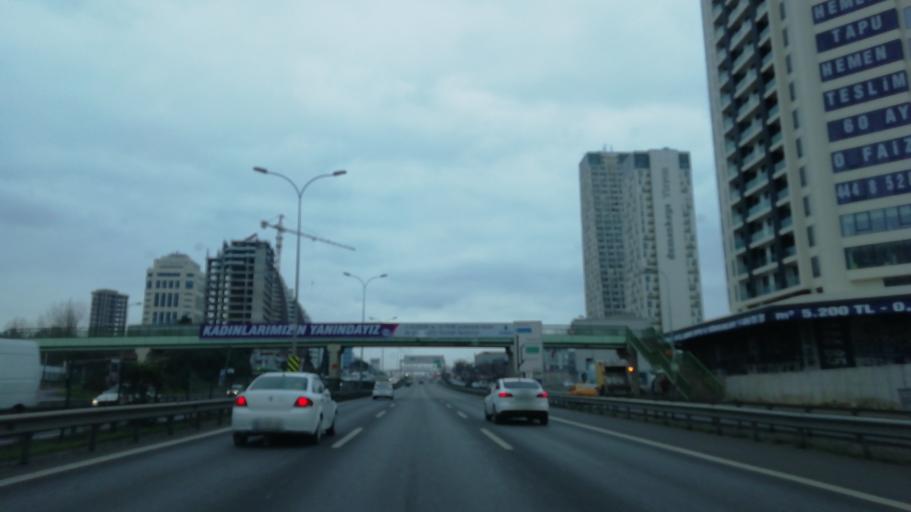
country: TR
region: Istanbul
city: Maltepe
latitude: 40.9112
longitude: 29.1962
